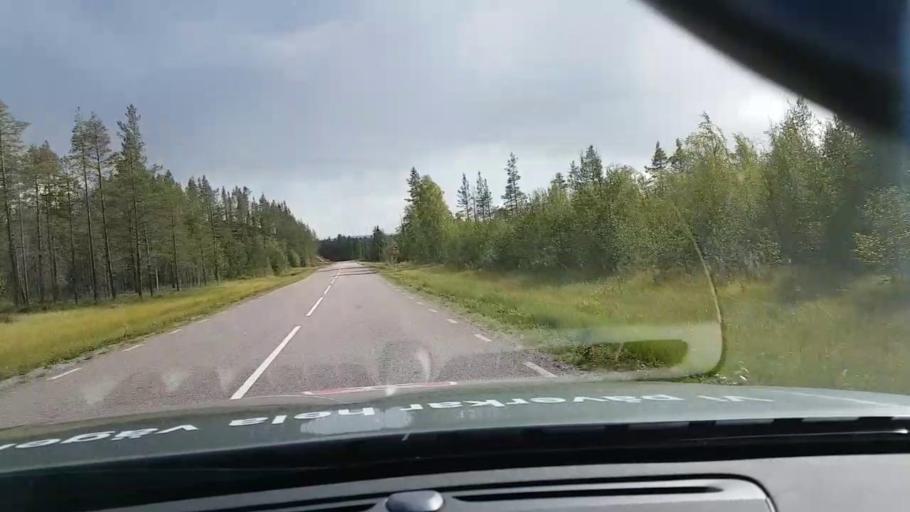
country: SE
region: Vaesterbotten
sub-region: Asele Kommun
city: Asele
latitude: 63.8705
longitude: 17.3575
